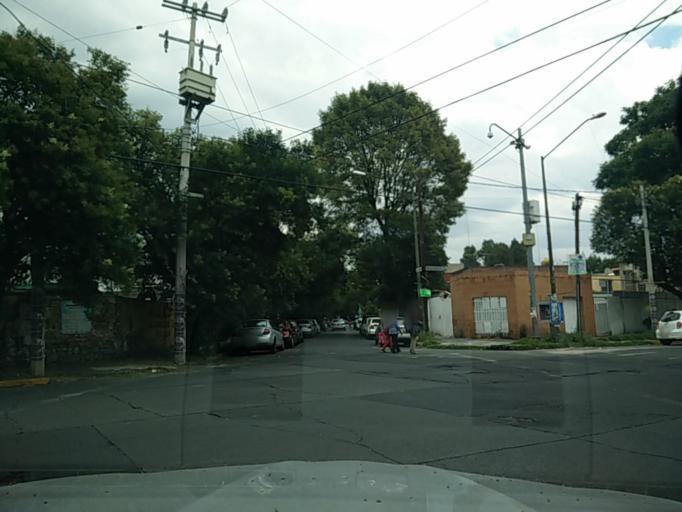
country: MX
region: Mexico City
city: Coyoacan
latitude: 19.3542
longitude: -99.1562
